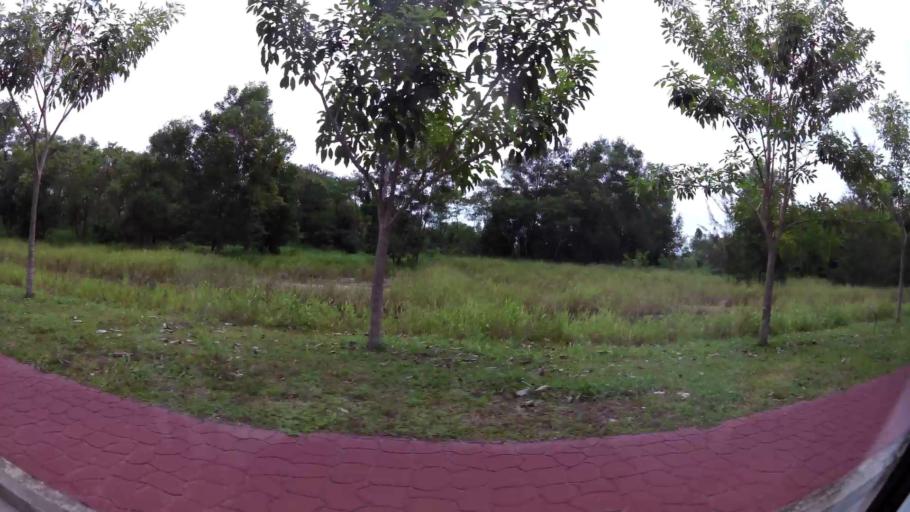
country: BN
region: Brunei and Muara
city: Bandar Seri Begawan
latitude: 4.9189
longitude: 114.9273
